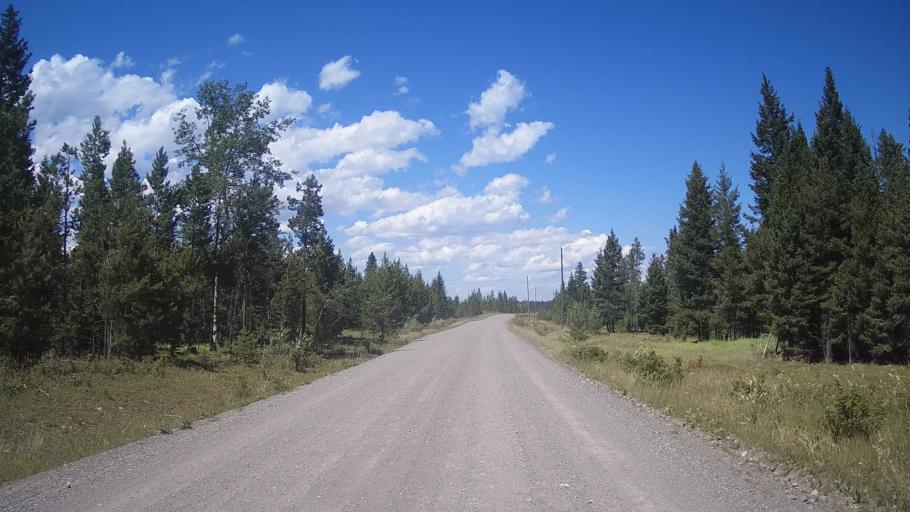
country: CA
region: British Columbia
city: Cache Creek
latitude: 51.2193
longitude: -121.6134
